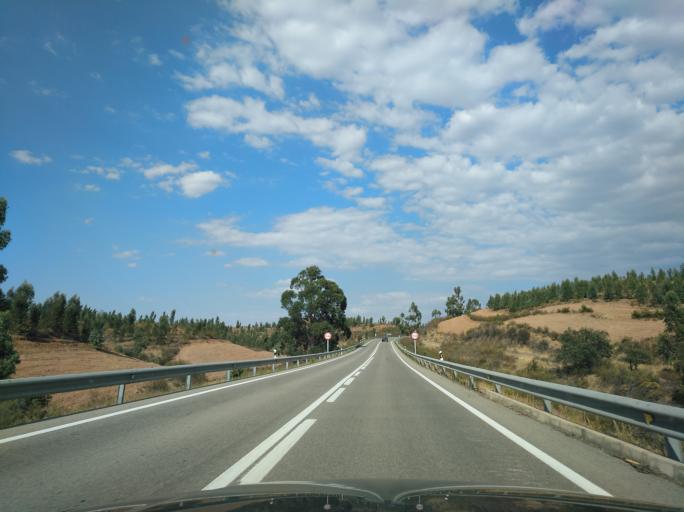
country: ES
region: Andalusia
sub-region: Provincia de Huelva
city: Rosal de la Frontera
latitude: 37.8815
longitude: -7.2095
